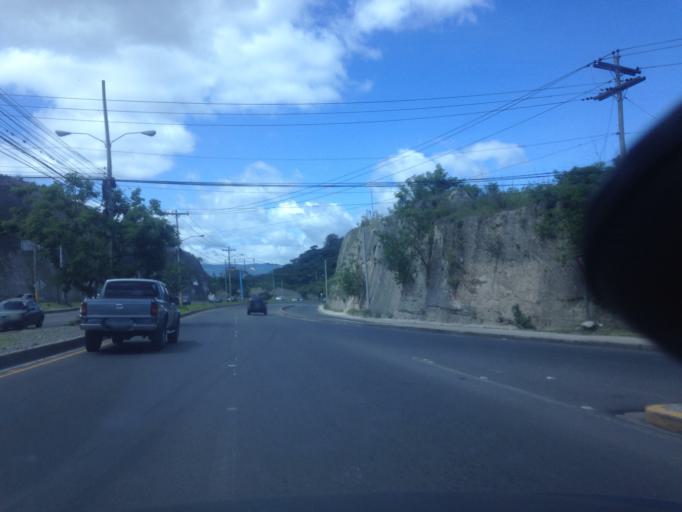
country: HN
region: Francisco Morazan
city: Yaguacire
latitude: 14.0489
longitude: -87.2126
